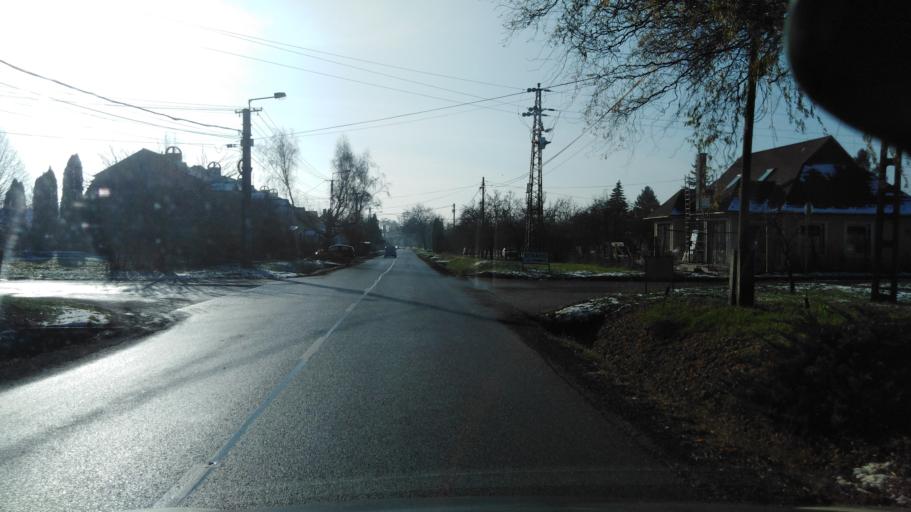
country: HU
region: Nograd
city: Paszto
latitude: 47.9290
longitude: 19.7036
